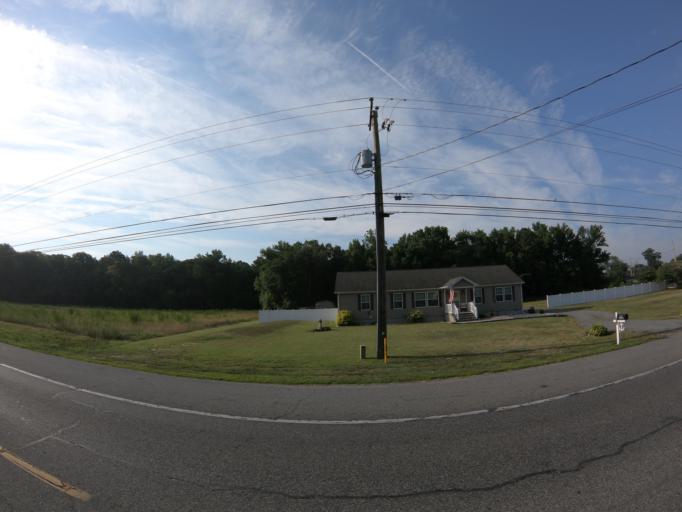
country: US
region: Delaware
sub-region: Sussex County
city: Millsboro
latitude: 38.5507
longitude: -75.2279
